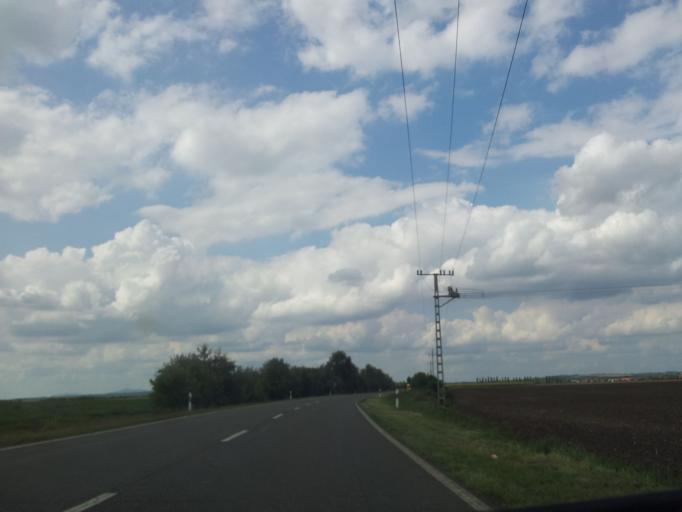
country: HU
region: Baranya
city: Mohacs
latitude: 45.9754
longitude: 18.6645
